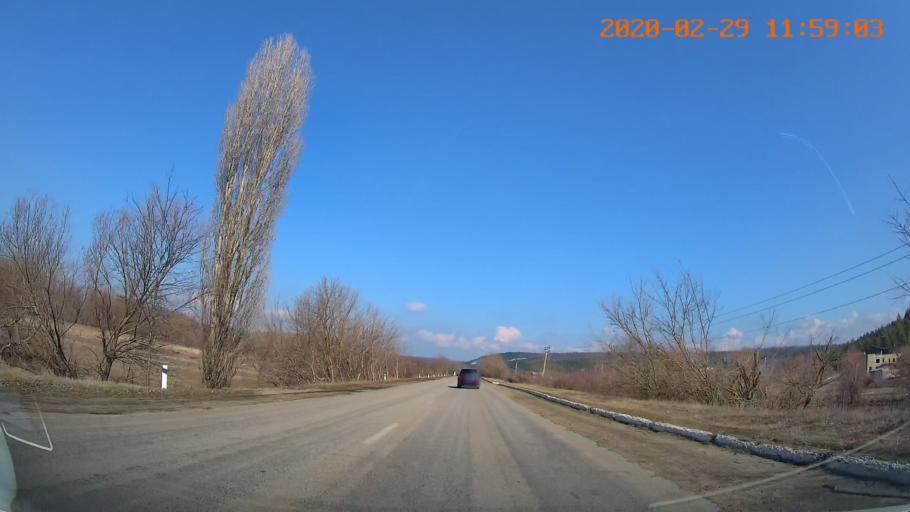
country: MD
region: Telenesti
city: Ribnita
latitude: 47.8207
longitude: 29.0147
